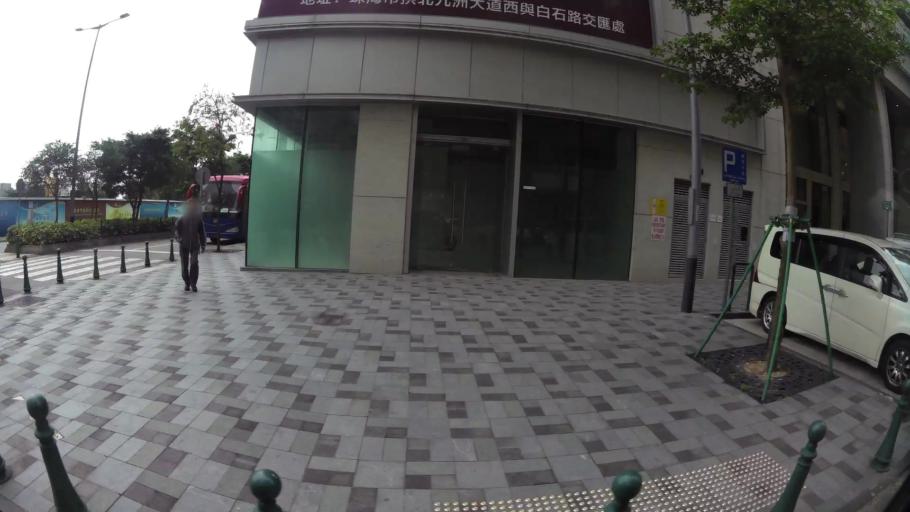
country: MO
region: Macau
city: Macau
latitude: 22.1878
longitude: 113.5531
